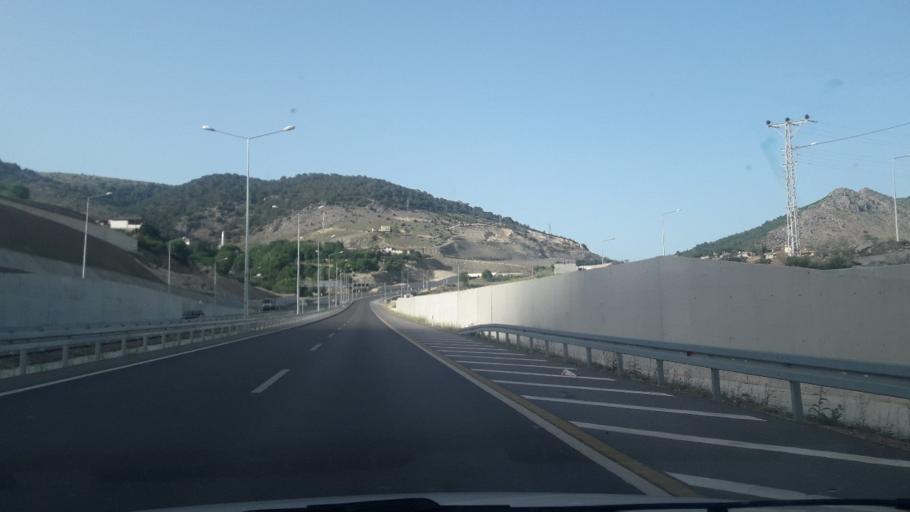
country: TR
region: Amasya
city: Amasya
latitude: 40.6589
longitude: 35.7874
